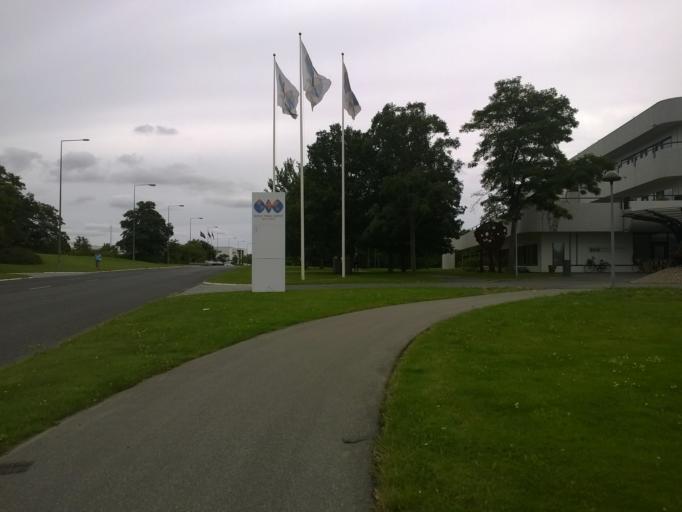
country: DK
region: Capital Region
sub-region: Ballerup Kommune
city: Ballerup
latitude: 55.7328
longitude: 12.3822
